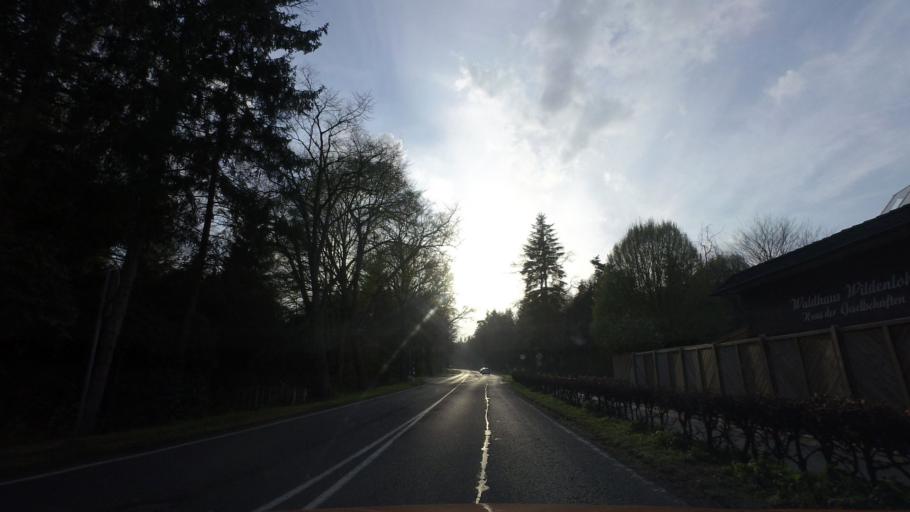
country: DE
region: Lower Saxony
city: Oldenburg
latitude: 53.1270
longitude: 8.1336
